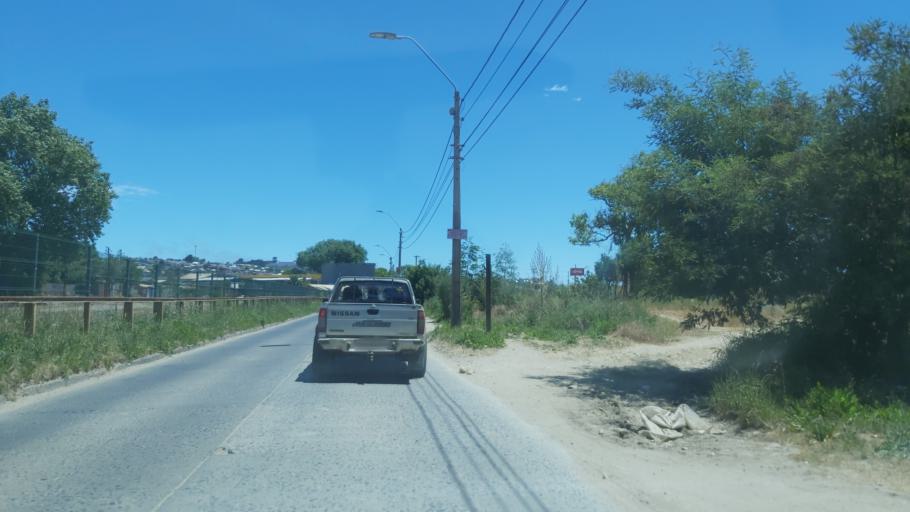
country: CL
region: Maule
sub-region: Provincia de Talca
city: Constitucion
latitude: -35.3380
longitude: -72.4016
